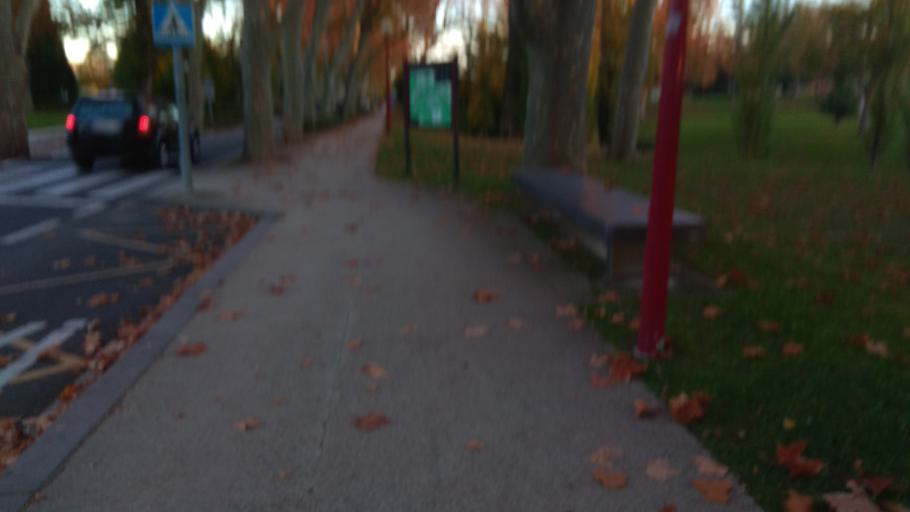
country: ES
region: Navarre
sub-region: Provincia de Navarra
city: Iturrama
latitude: 42.8005
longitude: -1.6599
